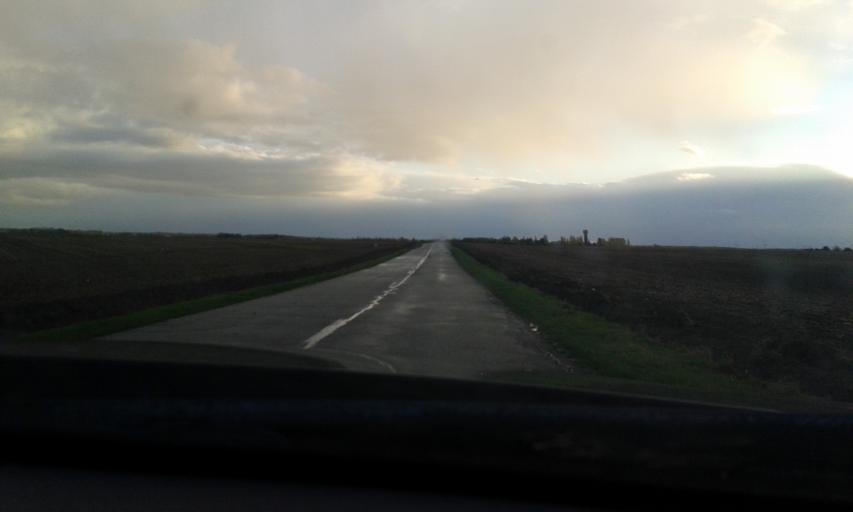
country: FR
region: Centre
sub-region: Departement du Loiret
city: Gidy
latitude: 48.0070
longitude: 1.8435
